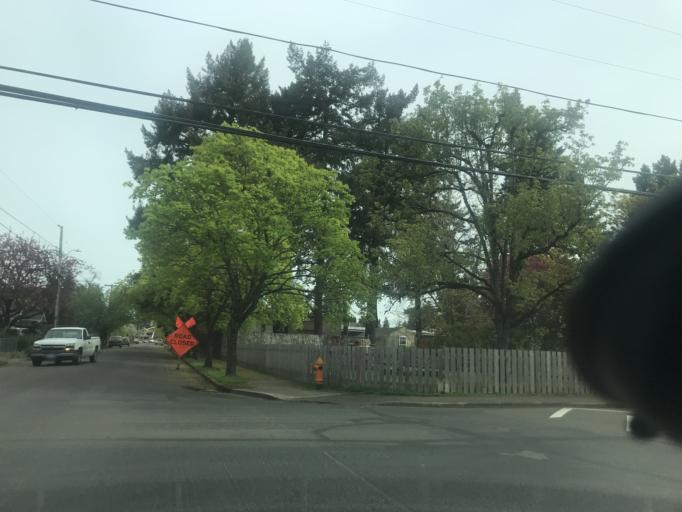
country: US
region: Oregon
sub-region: Multnomah County
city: Lents
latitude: 45.4937
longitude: -122.5880
